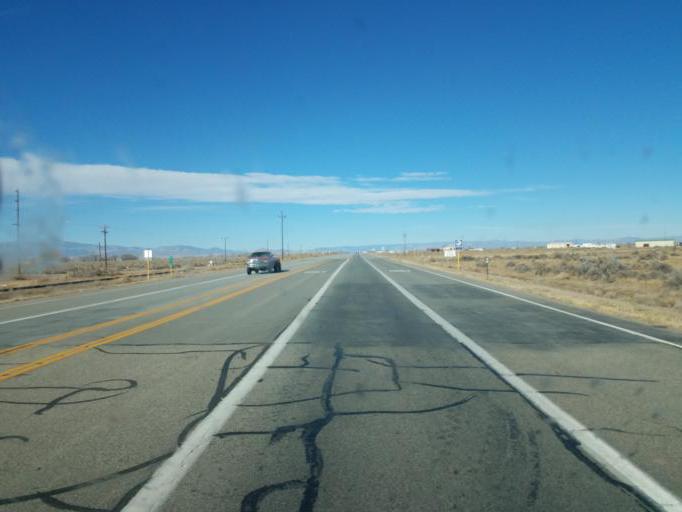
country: US
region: Colorado
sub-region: Alamosa County
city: Alamosa
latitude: 37.5127
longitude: -105.9829
